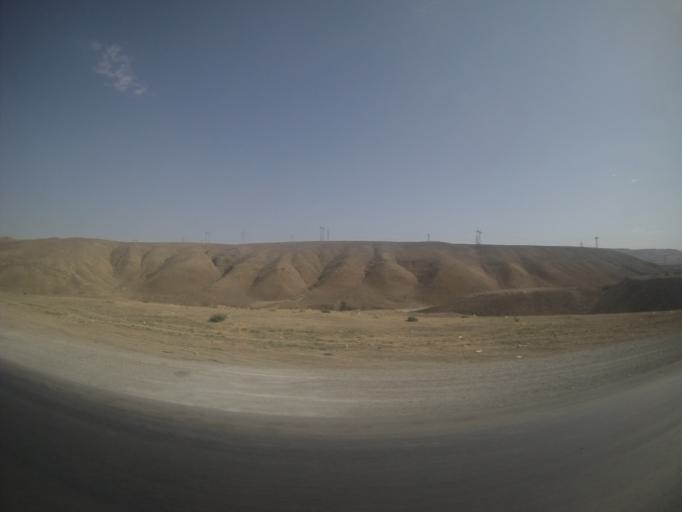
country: AZ
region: Qobustan
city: Qobustan
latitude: 40.4978
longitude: 49.0240
